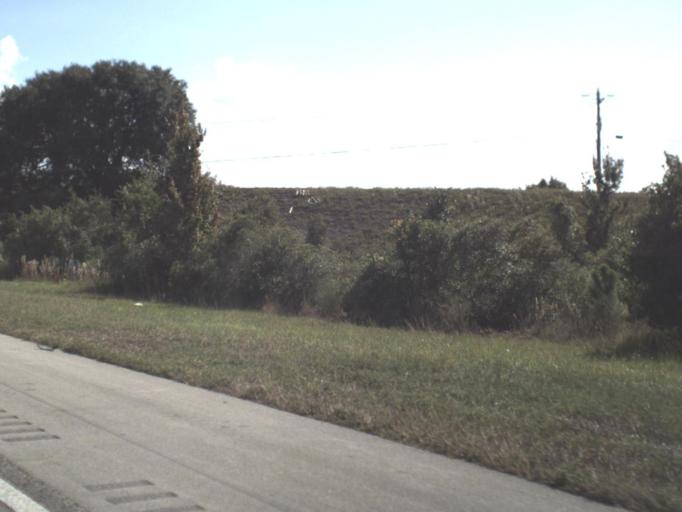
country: US
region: Florida
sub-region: Brevard County
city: June Park
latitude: 27.8775
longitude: -81.0248
